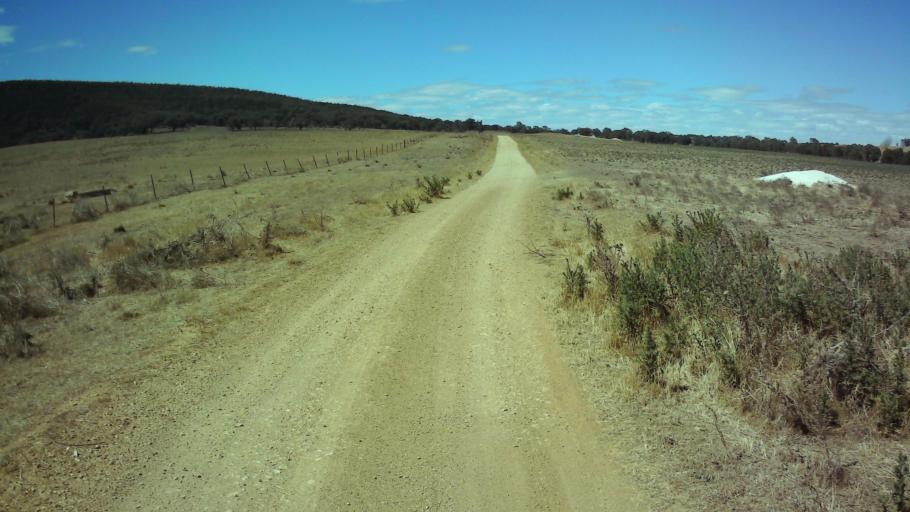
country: AU
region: New South Wales
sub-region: Weddin
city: Grenfell
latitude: -34.0352
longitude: 148.4341
